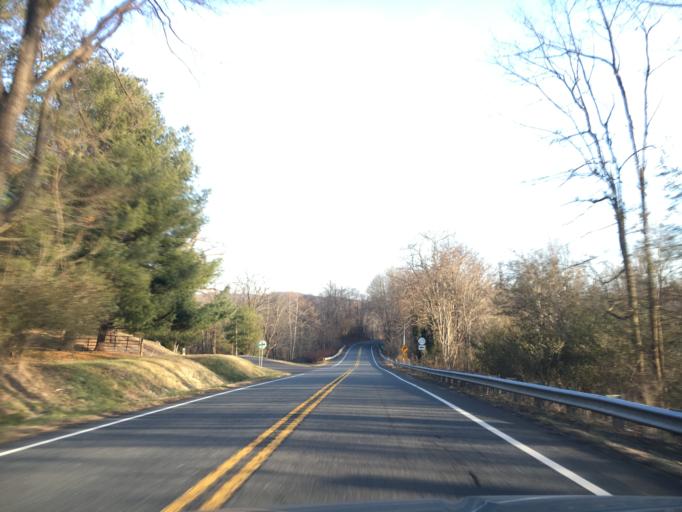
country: US
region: Virginia
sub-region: Rappahannock County
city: Washington
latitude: 38.6476
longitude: -78.2102
